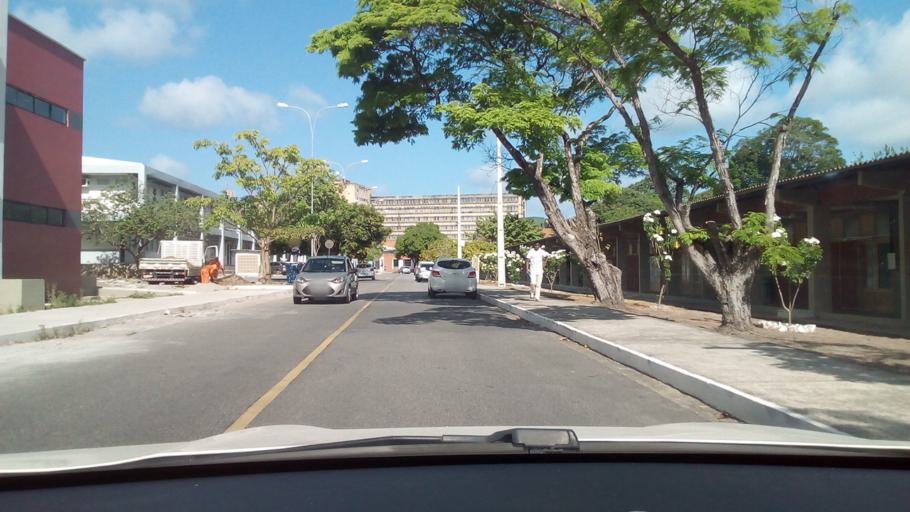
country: BR
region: Paraiba
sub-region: Joao Pessoa
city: Joao Pessoa
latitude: -7.1368
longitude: -34.8430
